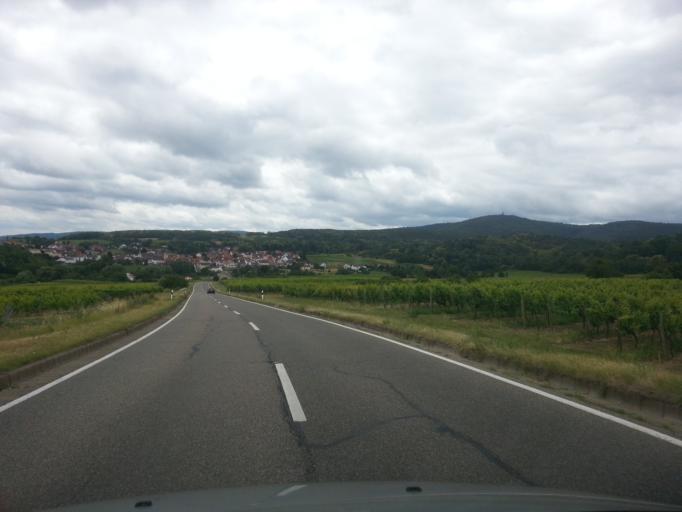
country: DE
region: Rheinland-Pfalz
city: Weisenheim am Berg
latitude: 49.5025
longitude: 8.1582
